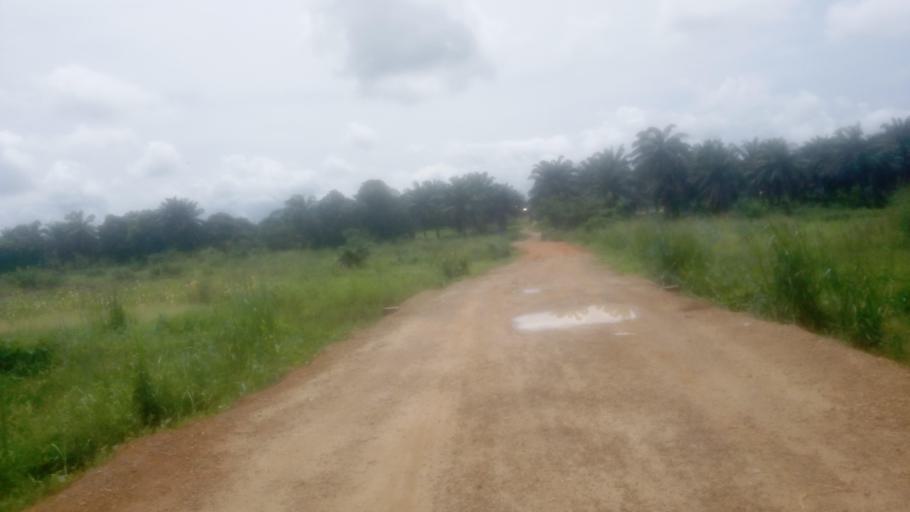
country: SL
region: Southern Province
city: Bo
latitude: 7.9574
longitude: -11.7124
